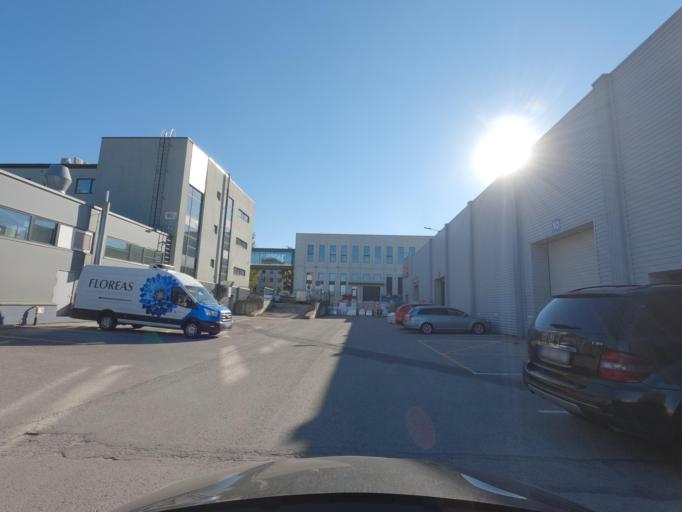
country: EE
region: Harju
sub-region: Tallinna linn
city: Tallinn
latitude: 59.4053
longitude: 24.7299
